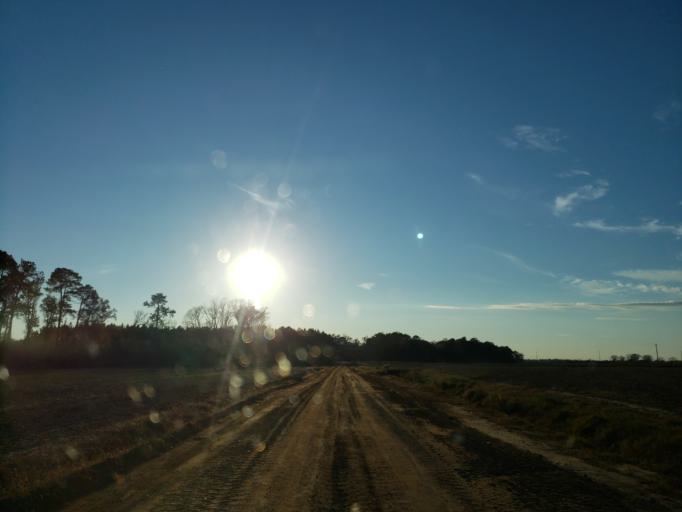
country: US
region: Georgia
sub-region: Dooly County
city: Vienna
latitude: 32.1412
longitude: -83.7468
